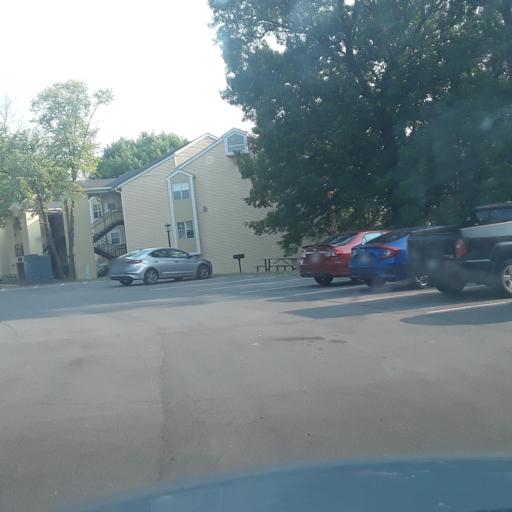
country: US
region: Tennessee
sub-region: Williamson County
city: Brentwood Estates
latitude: 36.0376
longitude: -86.7285
